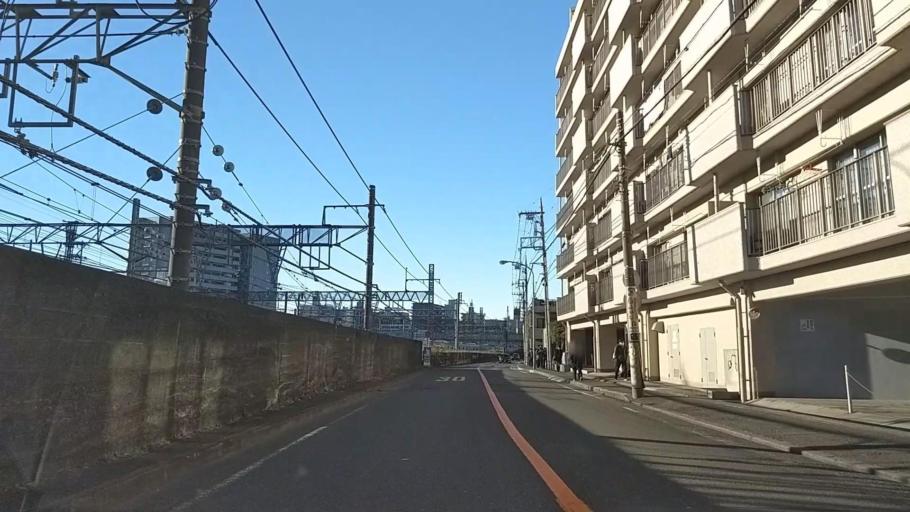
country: JP
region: Kanagawa
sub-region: Kawasaki-shi
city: Kawasaki
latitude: 35.5028
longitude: 139.6743
